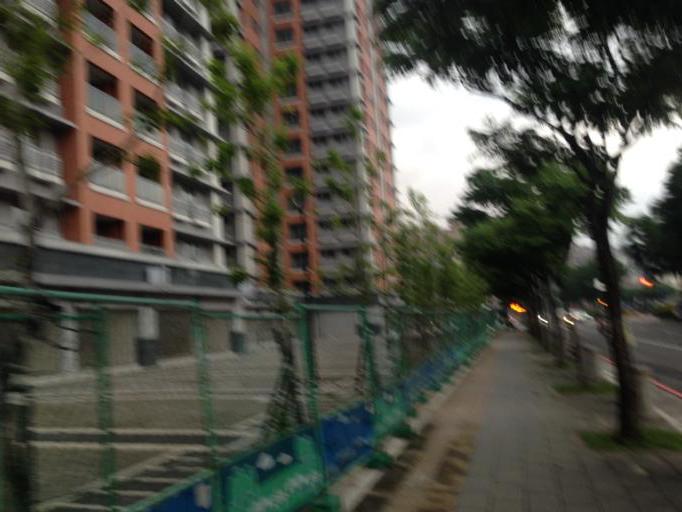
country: TW
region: Taiwan
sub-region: Taoyuan
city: Taoyuan
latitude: 24.9390
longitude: 121.3779
